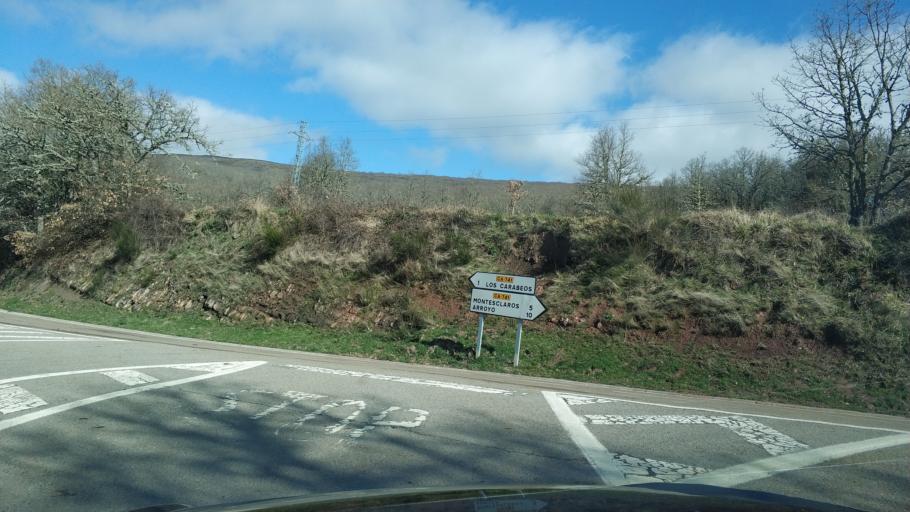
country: ES
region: Cantabria
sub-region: Provincia de Cantabria
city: Mataporquera
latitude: 42.9066
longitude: -4.0603
